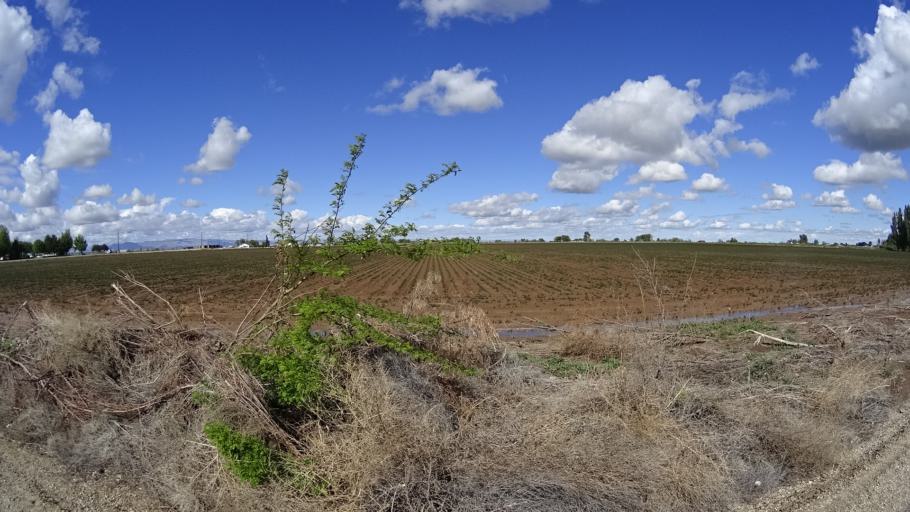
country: US
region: Idaho
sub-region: Ada County
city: Kuna
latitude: 43.4899
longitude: -116.4537
